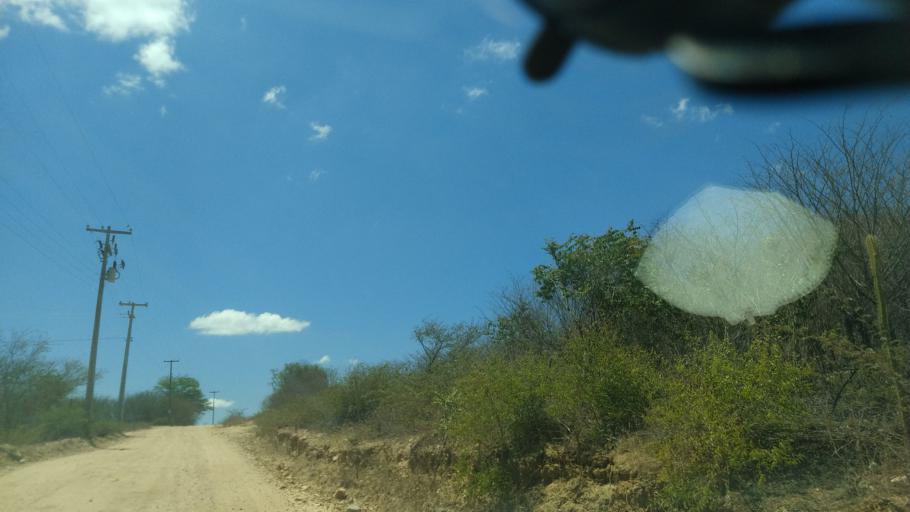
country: BR
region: Rio Grande do Norte
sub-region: Cerro Cora
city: Cerro Cora
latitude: -6.0247
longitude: -36.3346
